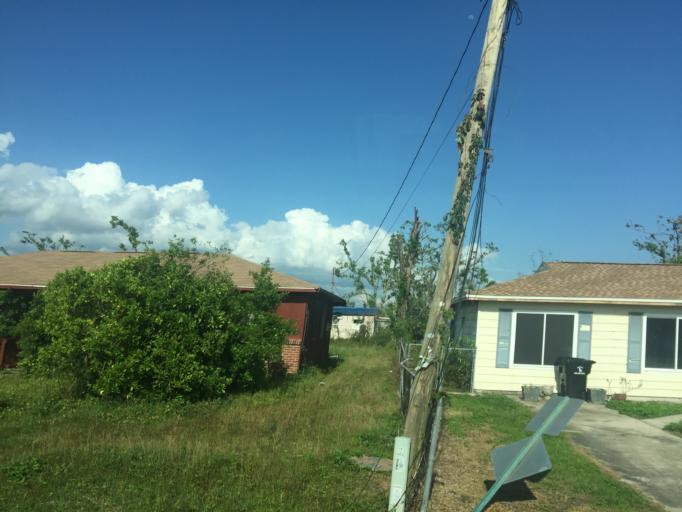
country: US
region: Florida
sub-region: Bay County
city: Cedar Grove
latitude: 30.1643
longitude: -85.6183
